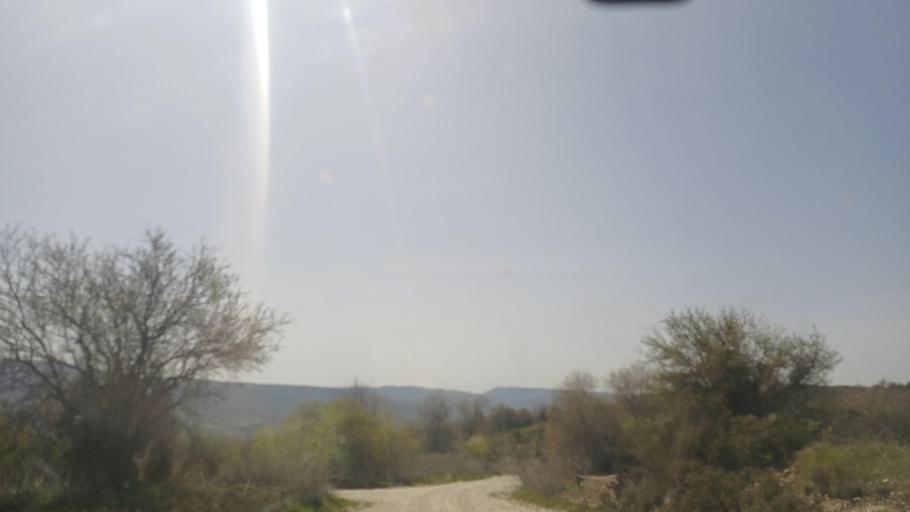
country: CY
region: Limassol
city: Pachna
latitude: 34.8687
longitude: 32.7124
